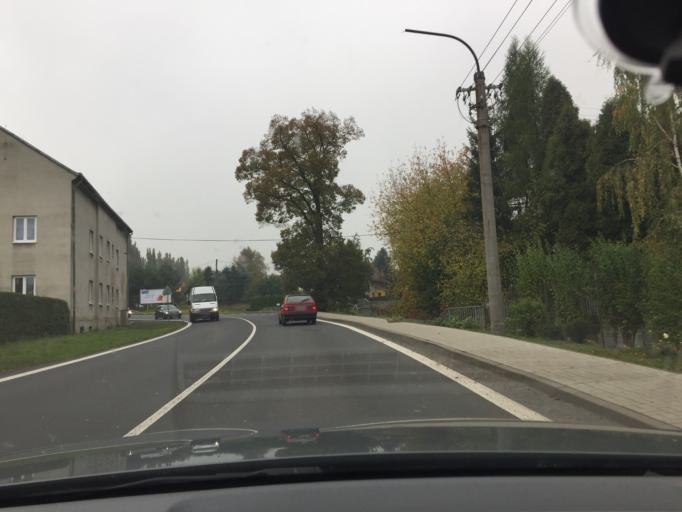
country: CZ
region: Ustecky
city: Libouchec
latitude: 50.7538
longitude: 14.0348
